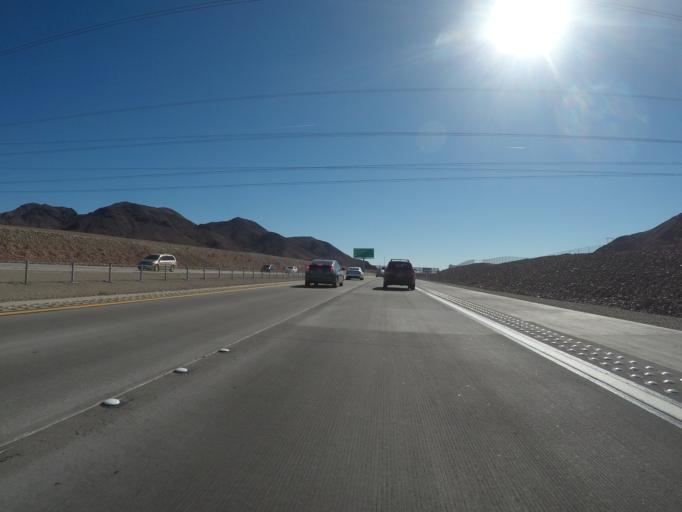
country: US
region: Nevada
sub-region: Clark County
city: Henderson
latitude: 35.9846
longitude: -114.9205
